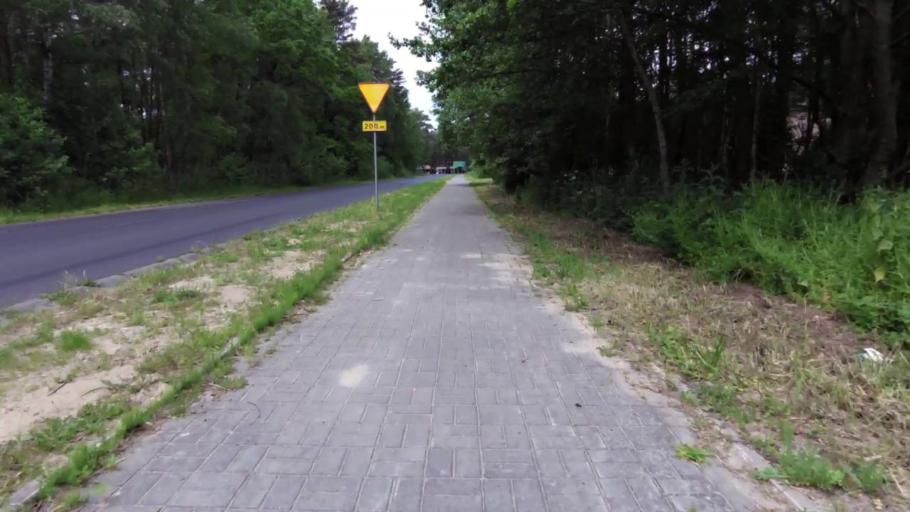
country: PL
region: West Pomeranian Voivodeship
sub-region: Powiat kamienski
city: Dziwnow
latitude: 53.9986
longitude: 14.6785
